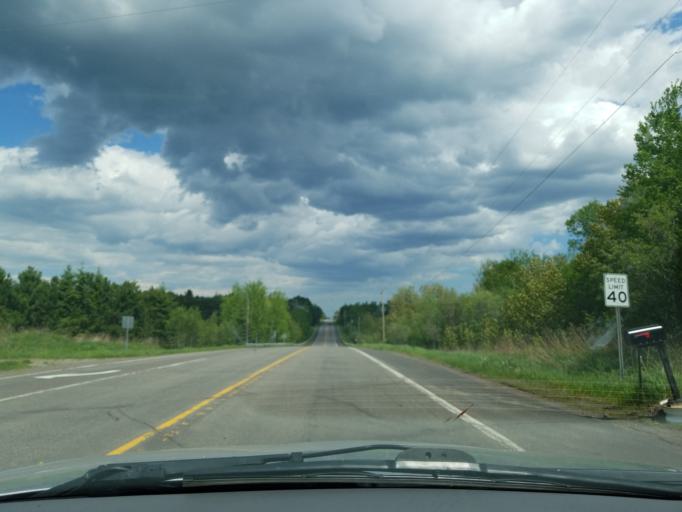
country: US
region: Minnesota
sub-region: Saint Louis County
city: Proctor
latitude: 46.7786
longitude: -92.2161
